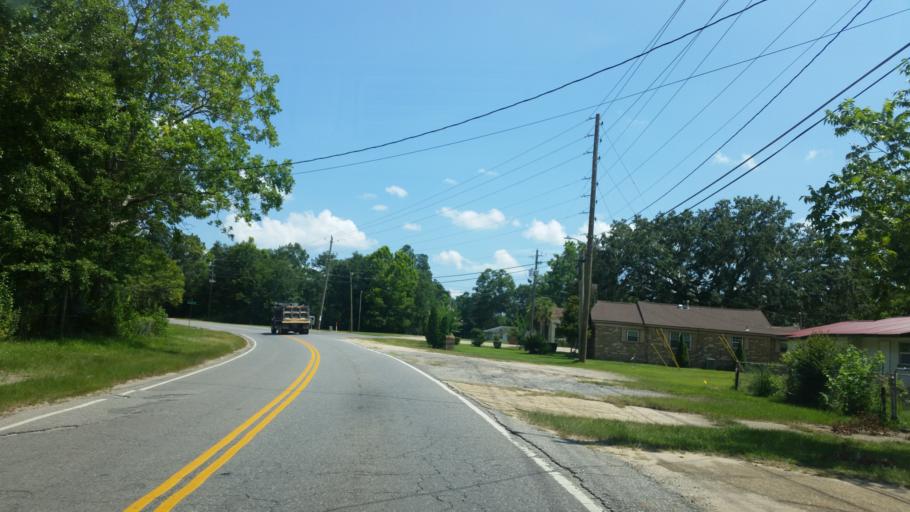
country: US
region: Florida
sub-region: Escambia County
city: Cantonment
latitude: 30.6044
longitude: -87.3319
